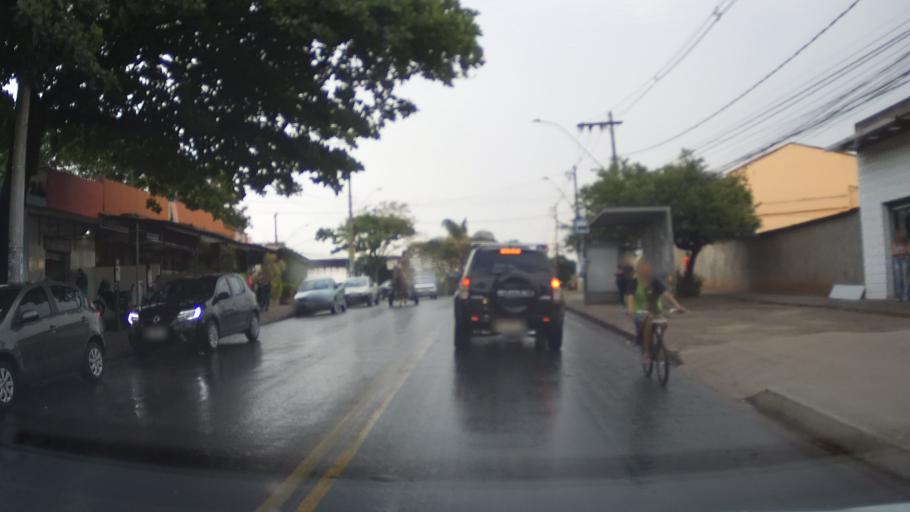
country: BR
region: Minas Gerais
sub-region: Belo Horizonte
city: Belo Horizonte
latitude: -19.9661
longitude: -43.9817
